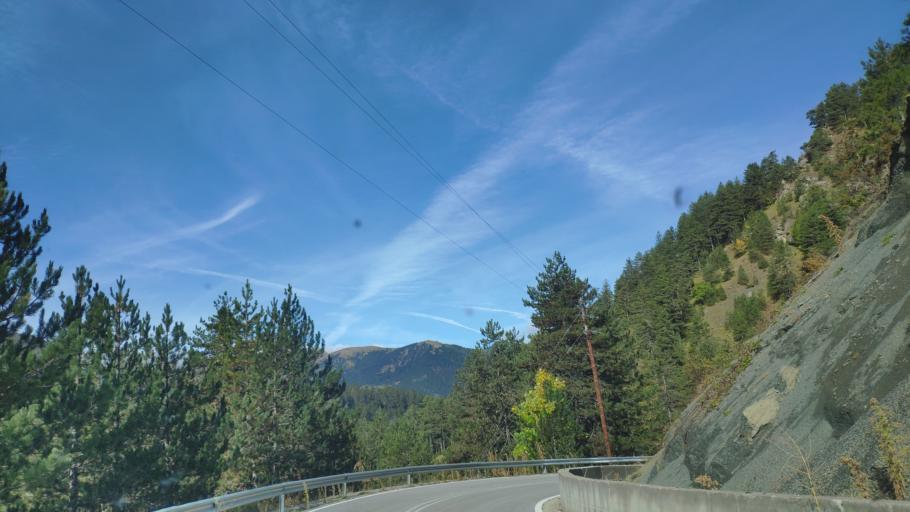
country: AL
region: Korce
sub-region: Rrethi i Devollit
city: Miras
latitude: 40.3981
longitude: 20.9020
